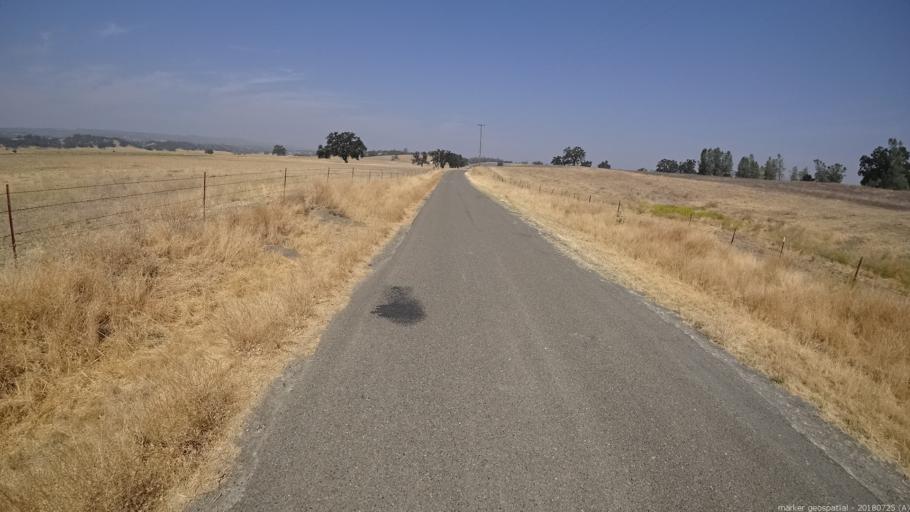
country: US
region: California
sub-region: San Luis Obispo County
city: Shandon
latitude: 35.8513
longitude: -120.3844
